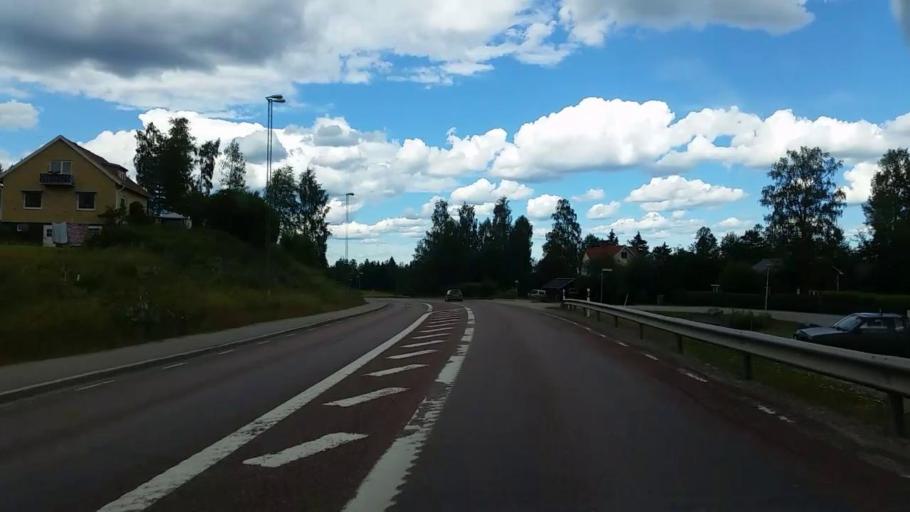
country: SE
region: Gaevleborg
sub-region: Ljusdals Kommun
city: Jaervsoe
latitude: 61.7013
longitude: 16.1649
